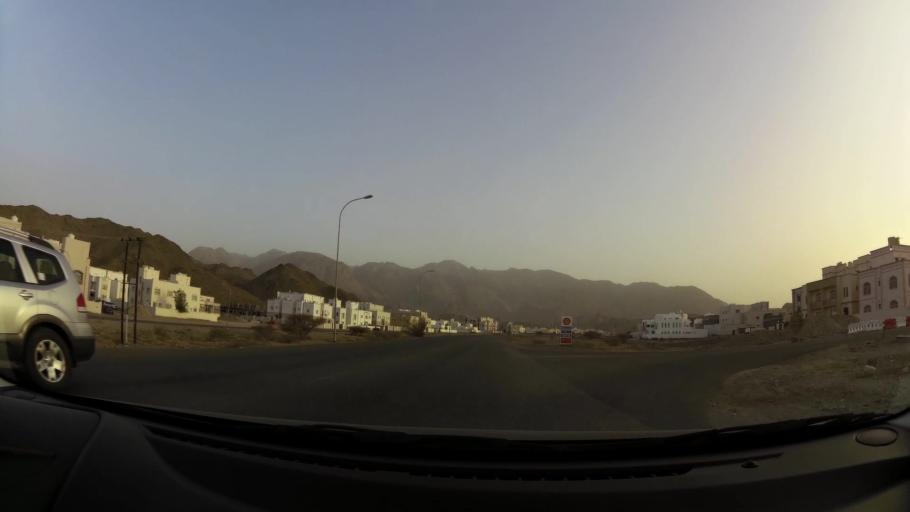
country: OM
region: Muhafazat Masqat
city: Bawshar
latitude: 23.4864
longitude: 58.3132
